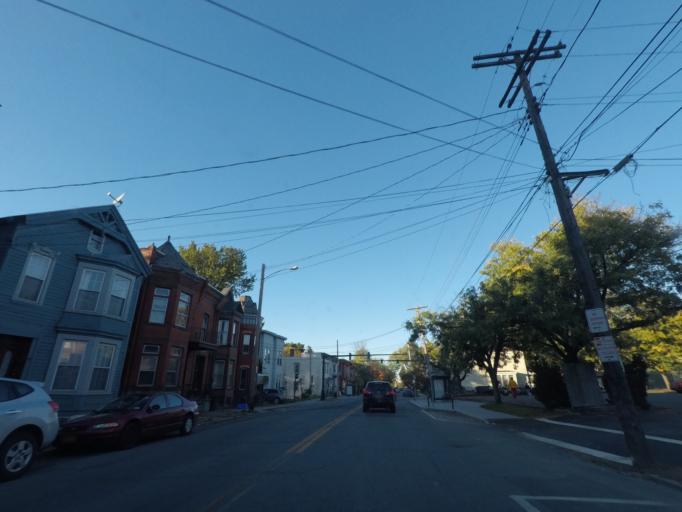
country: US
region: New York
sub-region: Albany County
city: Green Island
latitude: 42.7560
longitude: -73.6825
